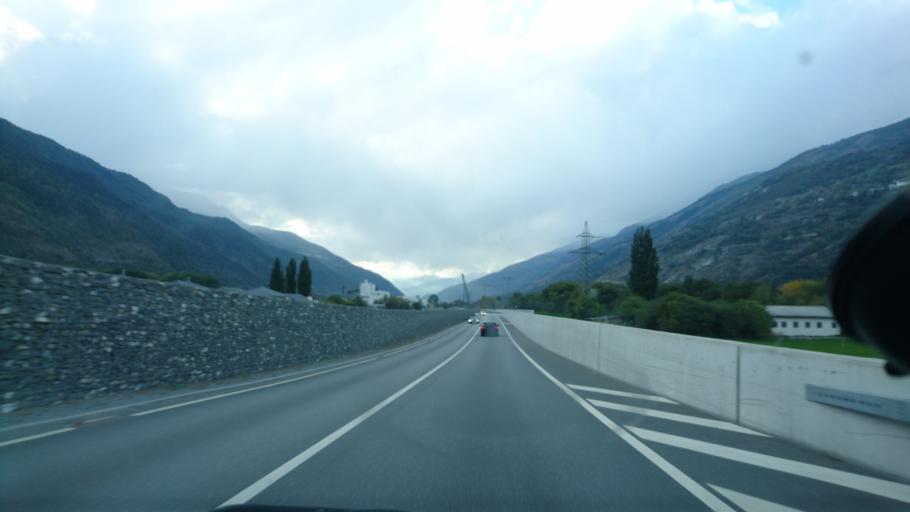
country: CH
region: Valais
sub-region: Visp District
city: Baltschieder
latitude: 46.3013
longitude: 7.8696
